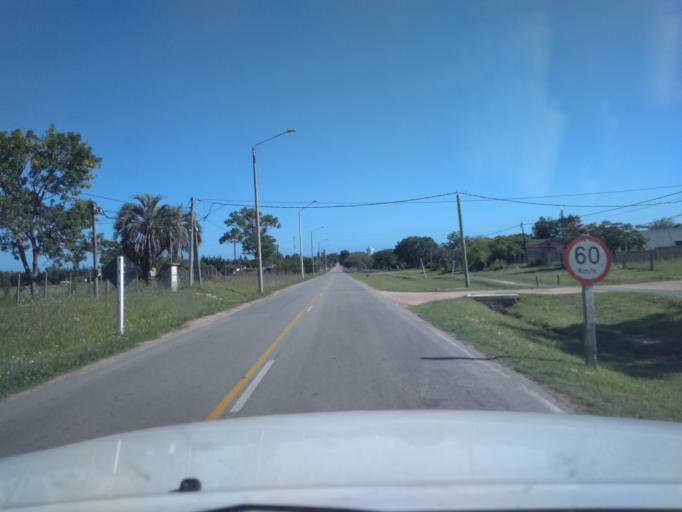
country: UY
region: Canelones
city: San Ramon
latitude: -34.3034
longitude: -55.9581
